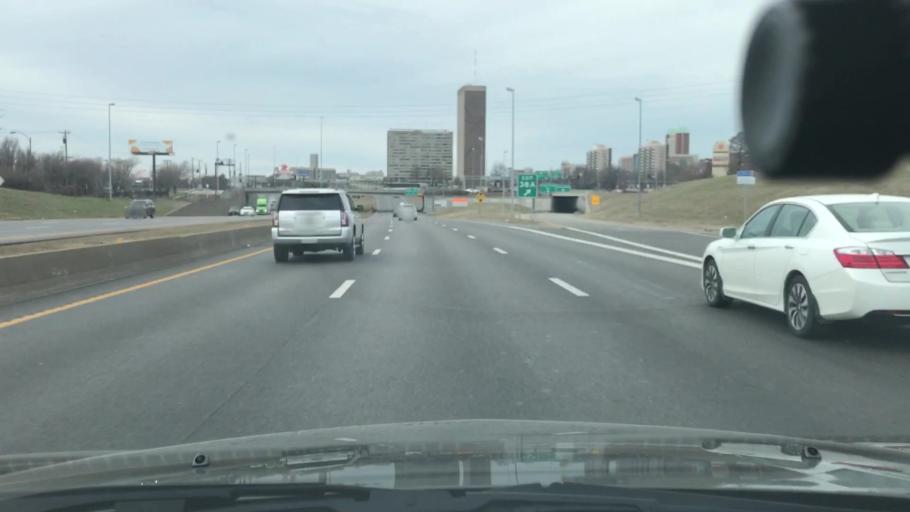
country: US
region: Missouri
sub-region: City of Saint Louis
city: St. Louis
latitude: 38.6298
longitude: -90.2244
